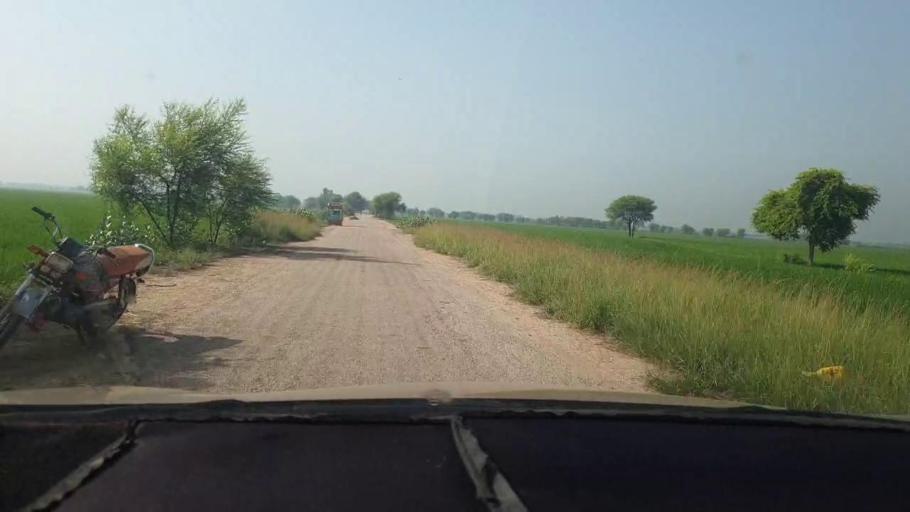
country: PK
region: Sindh
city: Kambar
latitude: 27.6283
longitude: 68.0895
